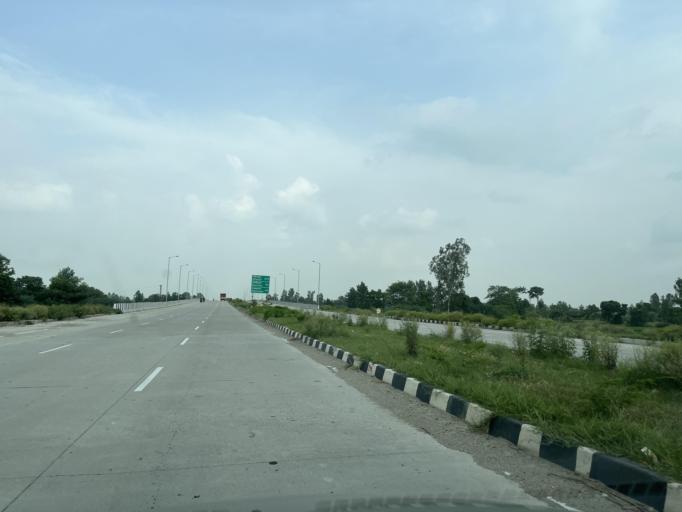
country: IN
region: Uttarakhand
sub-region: Udham Singh Nagar
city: Bazpur
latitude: 29.1484
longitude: 79.0525
